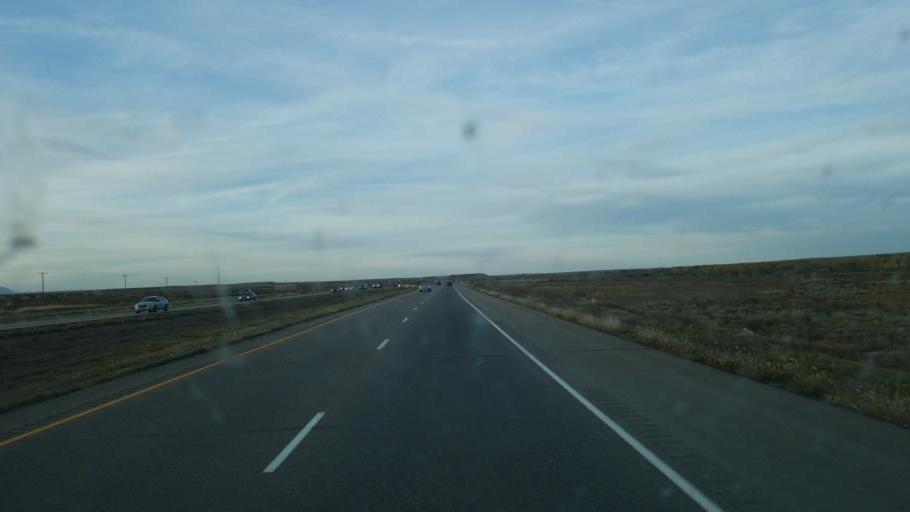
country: US
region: Colorado
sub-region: Pueblo County
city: Pueblo West
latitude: 38.3685
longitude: -104.6202
